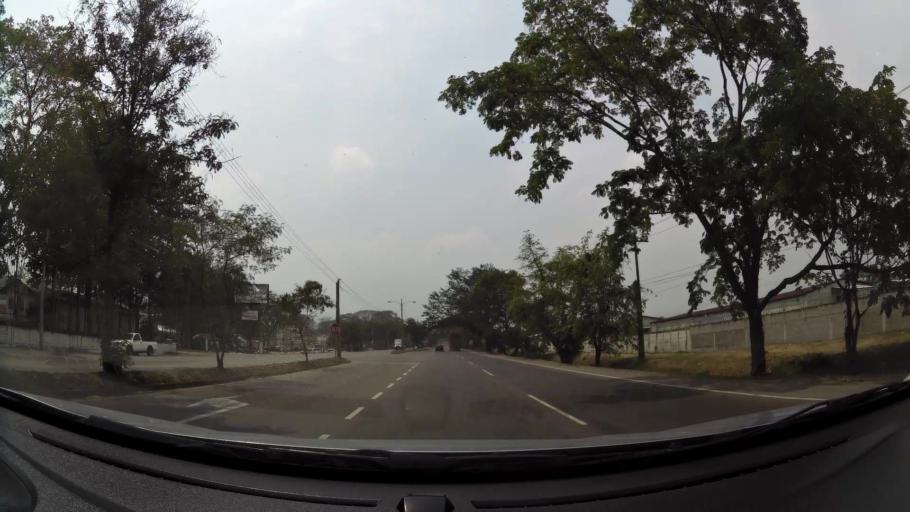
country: HN
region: Cortes
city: Chotepe
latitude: 15.3951
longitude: -87.9948
